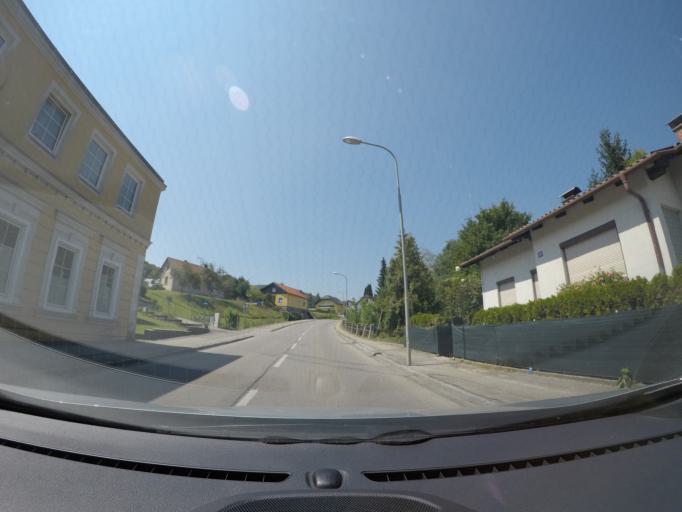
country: AT
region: Lower Austria
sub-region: Politischer Bezirk Sankt Polten
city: Eichgraben
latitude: 48.1843
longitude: 15.9600
